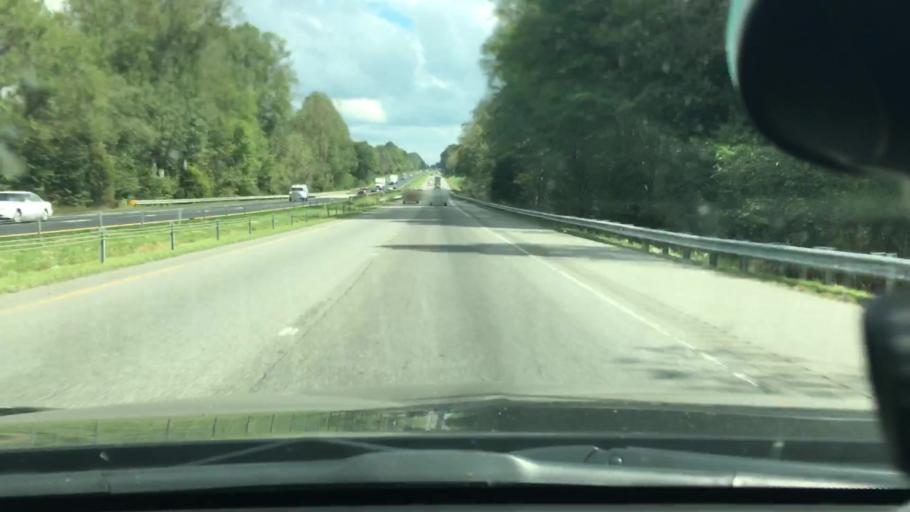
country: US
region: North Carolina
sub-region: Iredell County
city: Statesville
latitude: 35.7858
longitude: -80.9600
